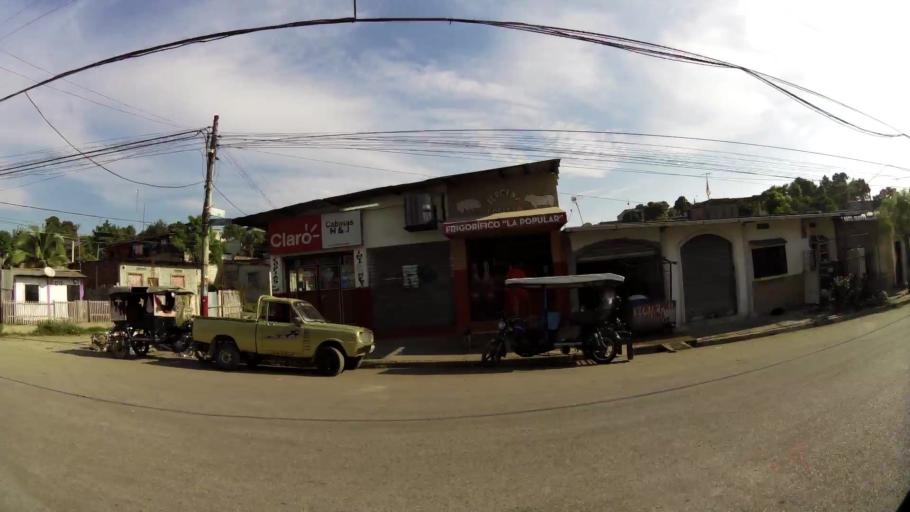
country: EC
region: Guayas
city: Eloy Alfaro
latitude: -2.0757
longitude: -79.9297
